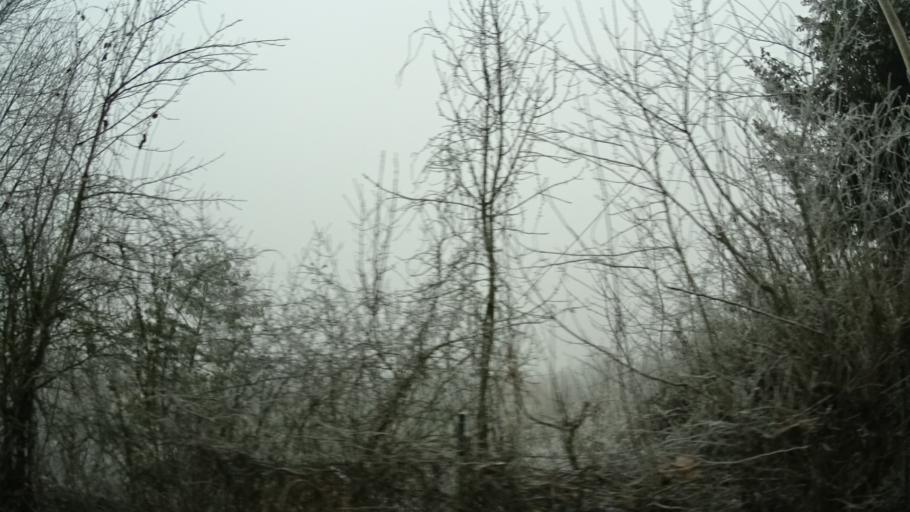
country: DE
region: Bavaria
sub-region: Regierungsbezirk Unterfranken
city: Hassfurt
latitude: 50.0810
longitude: 10.5735
